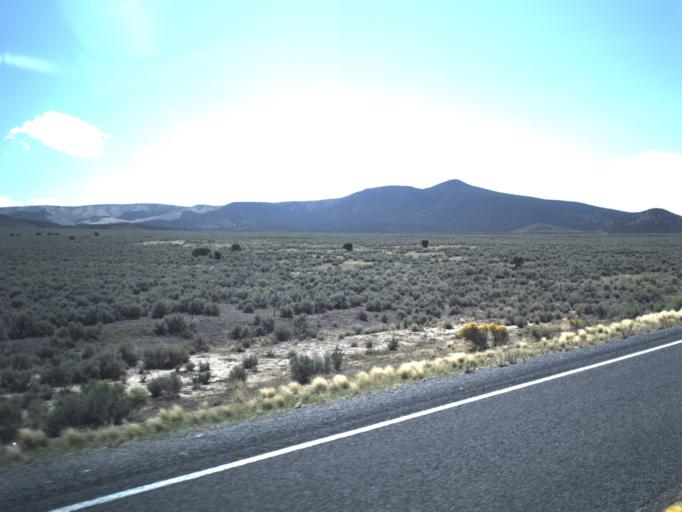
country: US
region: Utah
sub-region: Beaver County
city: Milford
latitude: 38.1950
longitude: -112.9350
